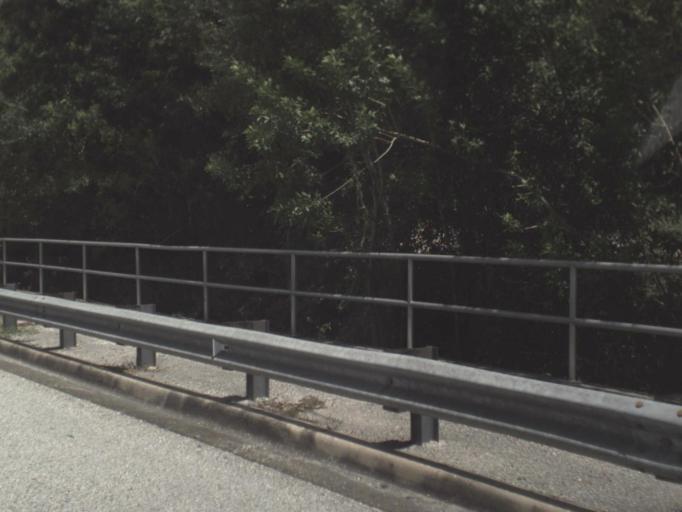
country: US
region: Florida
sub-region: Pasco County
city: Trinity
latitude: 28.1643
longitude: -82.6977
